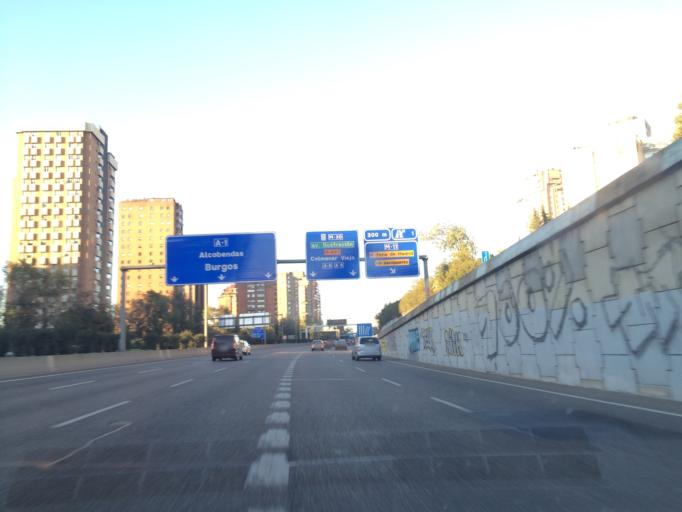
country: ES
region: Madrid
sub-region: Provincia de Madrid
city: Pinar de Chamartin
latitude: 40.4764
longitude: -3.6742
